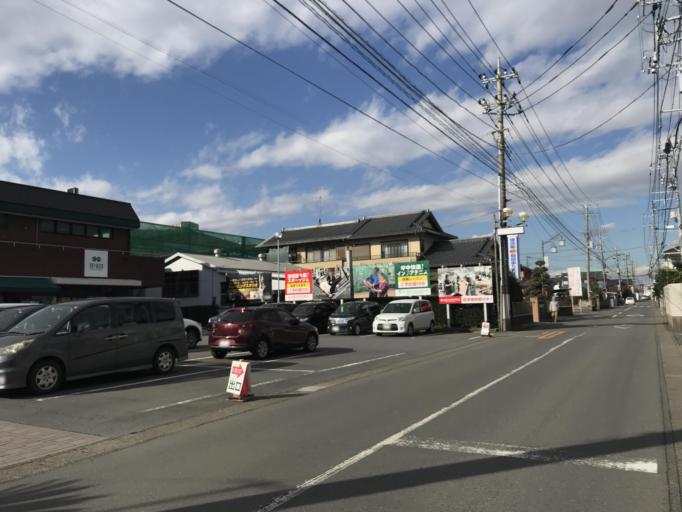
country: JP
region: Ibaraki
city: Ushiku
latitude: 35.9728
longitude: 140.1481
